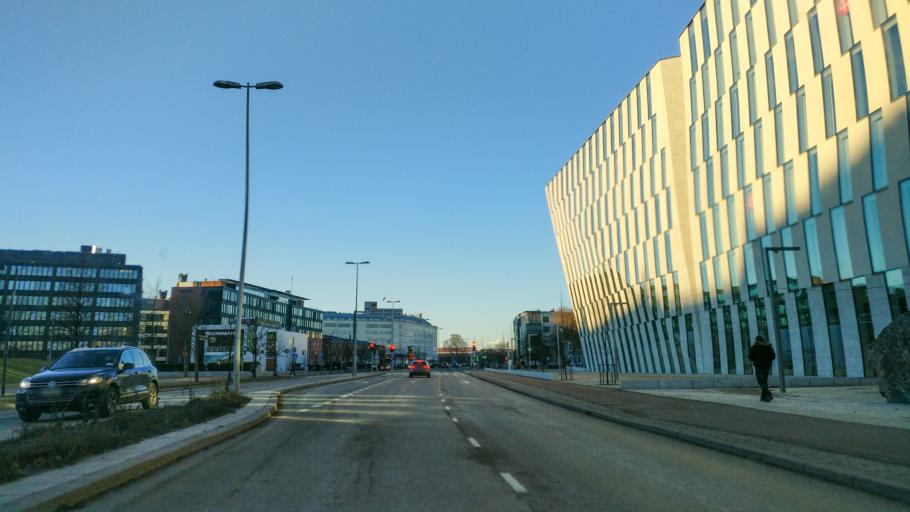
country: FI
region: Uusimaa
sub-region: Helsinki
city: Helsinki
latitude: 60.1902
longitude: 24.9589
